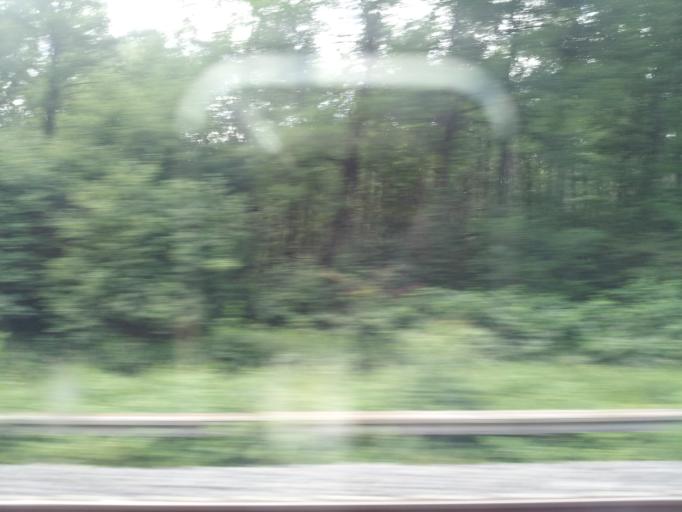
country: DE
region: Baden-Wuerttemberg
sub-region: Karlsruhe Region
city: Weingarten
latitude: 49.0392
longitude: 8.5025
